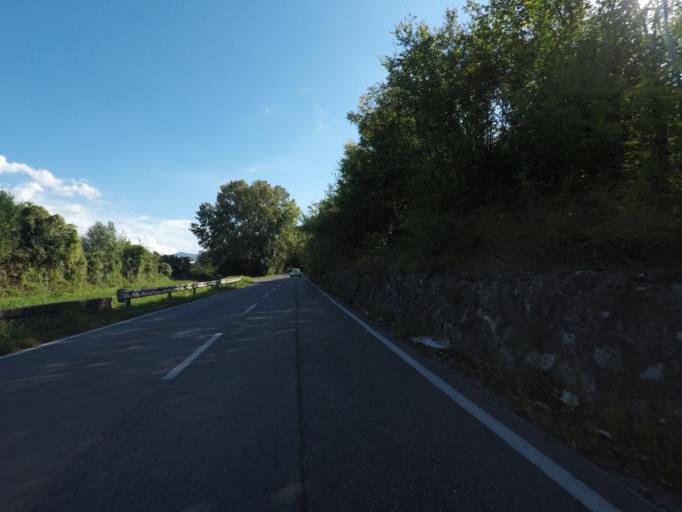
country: IT
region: Tuscany
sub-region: Provincia di Lucca
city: Lucca
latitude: 43.8744
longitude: 10.5209
